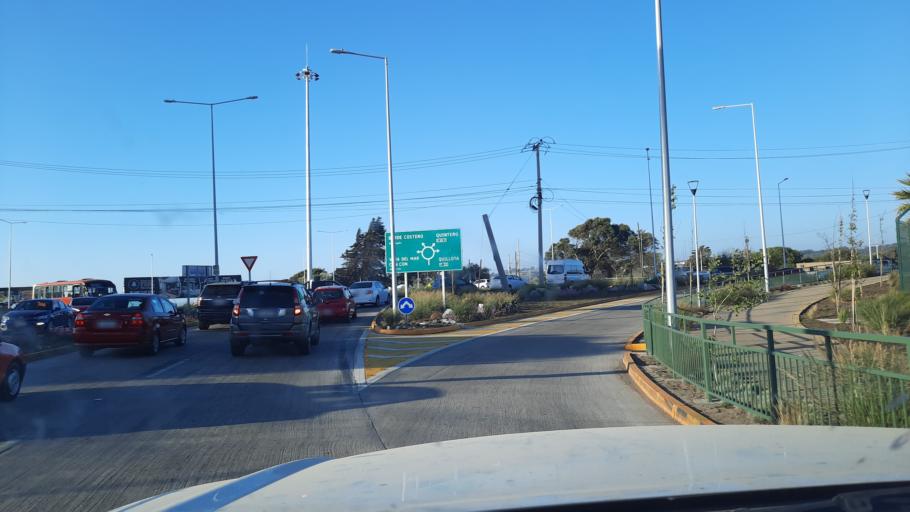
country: CL
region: Valparaiso
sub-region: Provincia de Valparaiso
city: Vina del Mar
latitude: -32.9222
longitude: -71.5069
